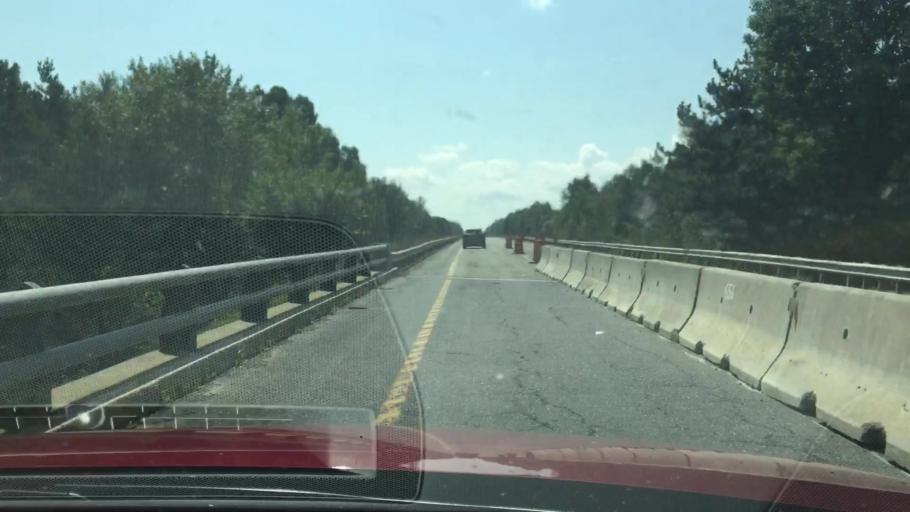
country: US
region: Maine
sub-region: Penobscot County
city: Patten
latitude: 45.8671
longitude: -68.4170
